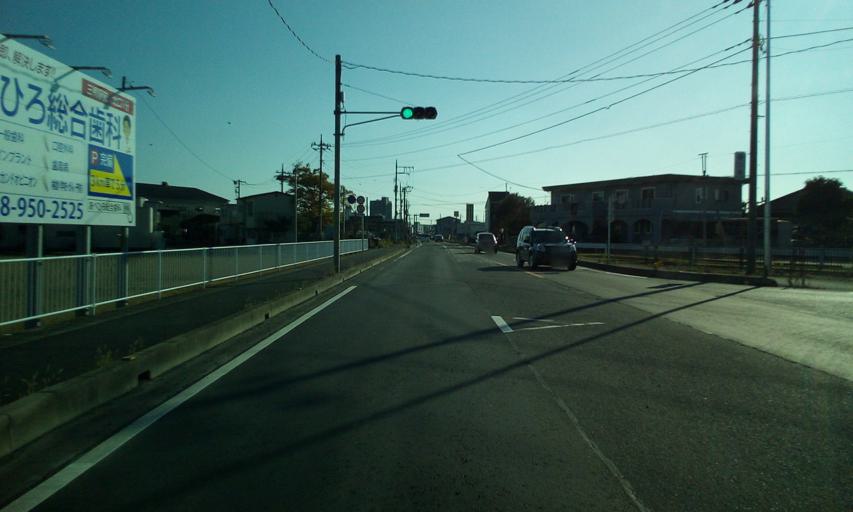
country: JP
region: Chiba
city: Nagareyama
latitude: 35.8678
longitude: 139.8882
